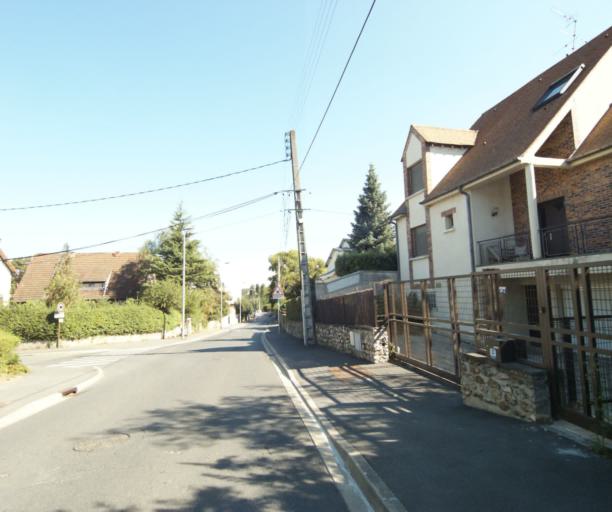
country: FR
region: Ile-de-France
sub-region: Departement de Seine-et-Marne
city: Gouvernes
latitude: 48.8717
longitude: 2.7003
